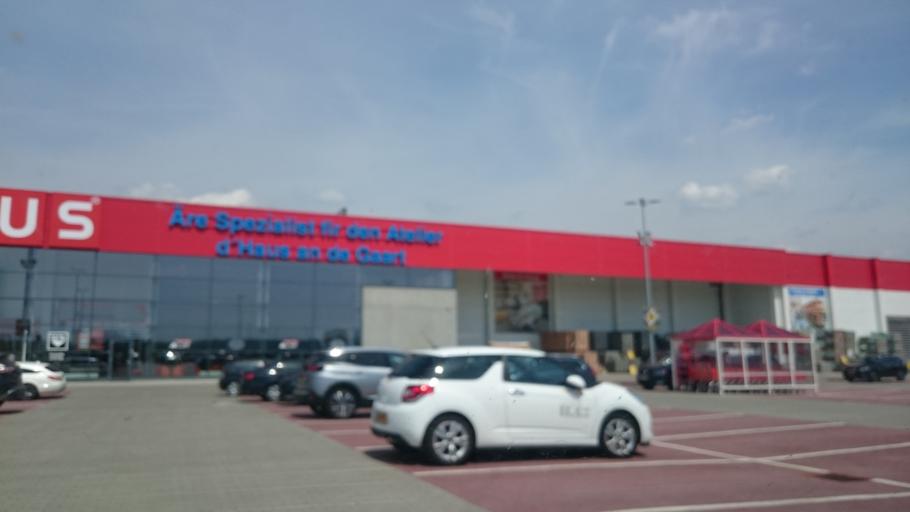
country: LU
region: Luxembourg
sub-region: Canton de Capellen
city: Mamer
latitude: 49.6399
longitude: 6.0154
